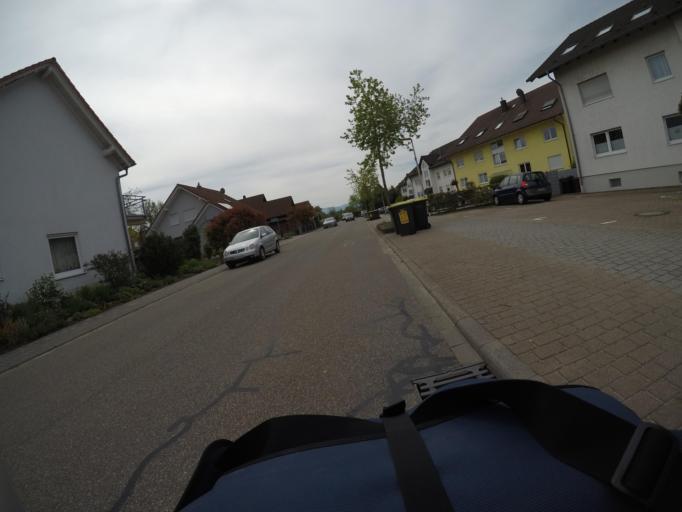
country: DE
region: Baden-Wuerttemberg
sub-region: Karlsruhe Region
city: Hugelsheim
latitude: 48.7930
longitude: 8.1098
